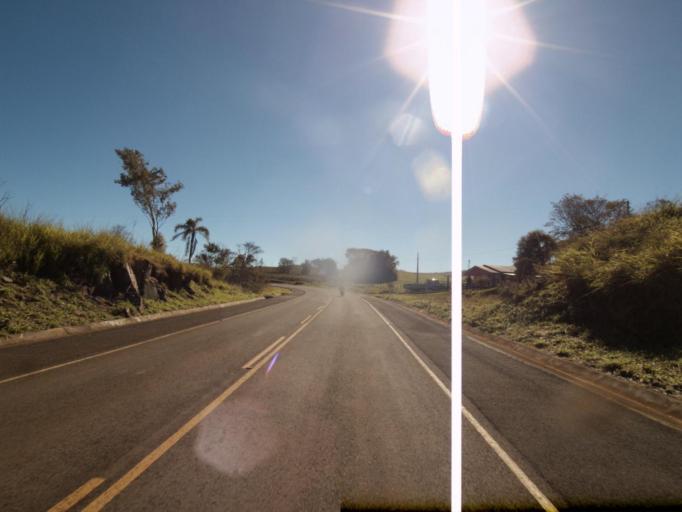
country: AR
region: Misiones
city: Bernardo de Irigoyen
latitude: -26.6110
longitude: -53.6893
